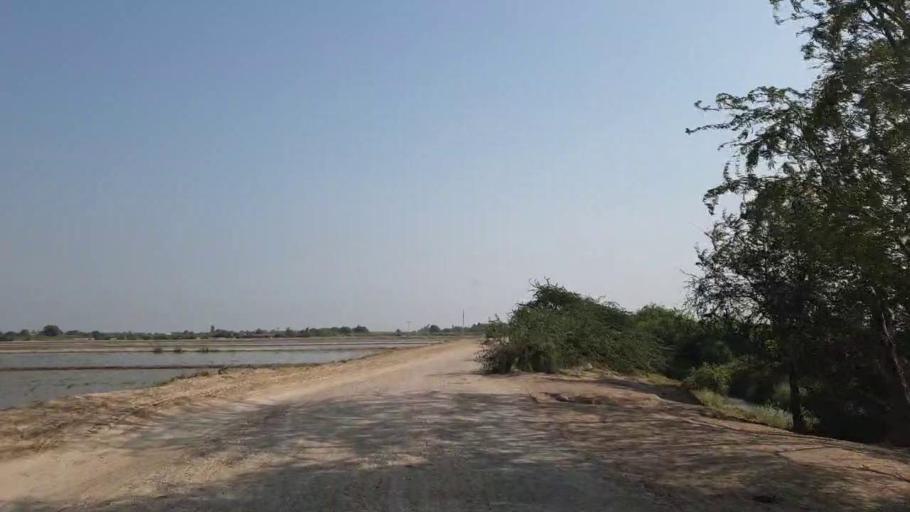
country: PK
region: Sindh
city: Bulri
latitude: 24.9343
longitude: 68.3670
